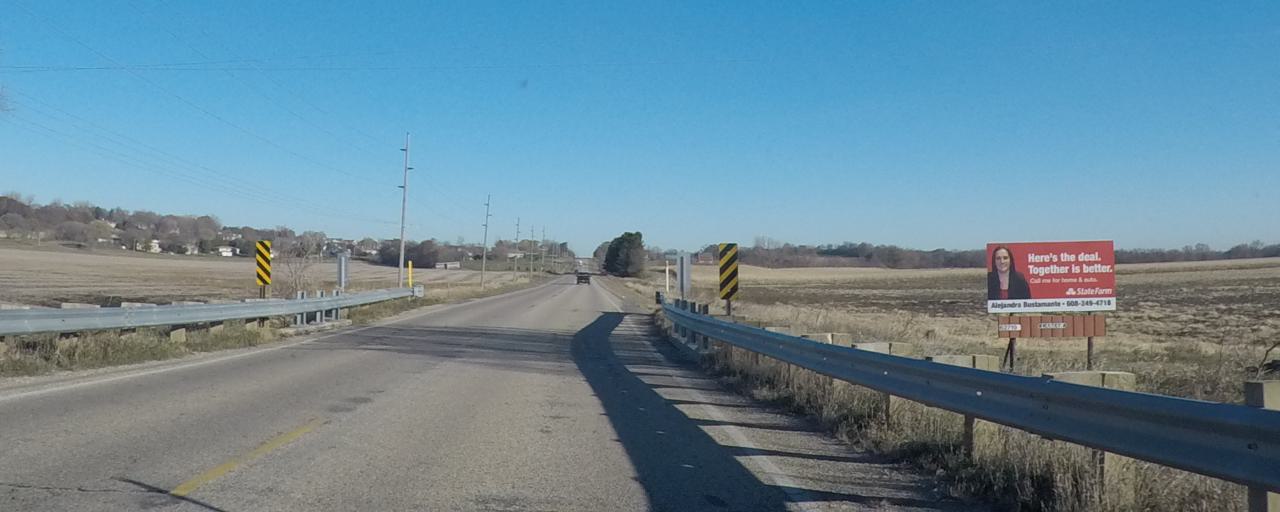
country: US
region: Wisconsin
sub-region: Dane County
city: Cottage Grove
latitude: 43.0400
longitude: -89.1999
